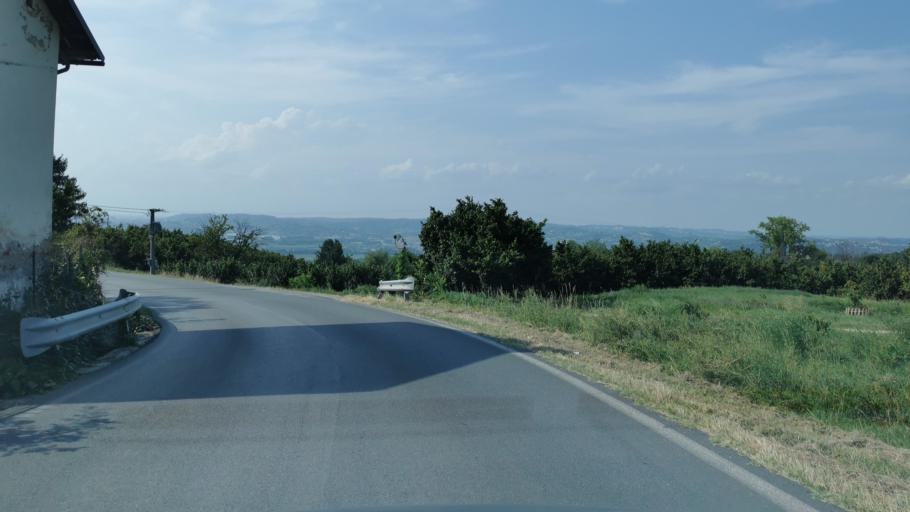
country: IT
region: Piedmont
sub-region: Provincia di Cuneo
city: La Morra
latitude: 44.6448
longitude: 7.9171
